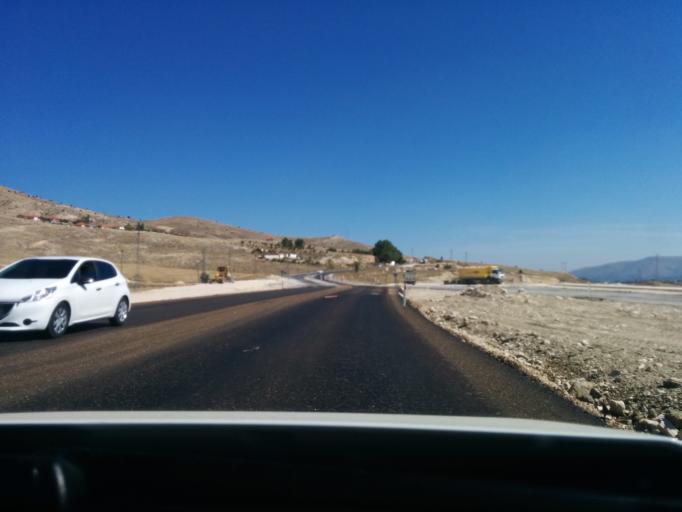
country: TR
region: Antalya
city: Kizilcadag
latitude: 37.0327
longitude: 29.9903
